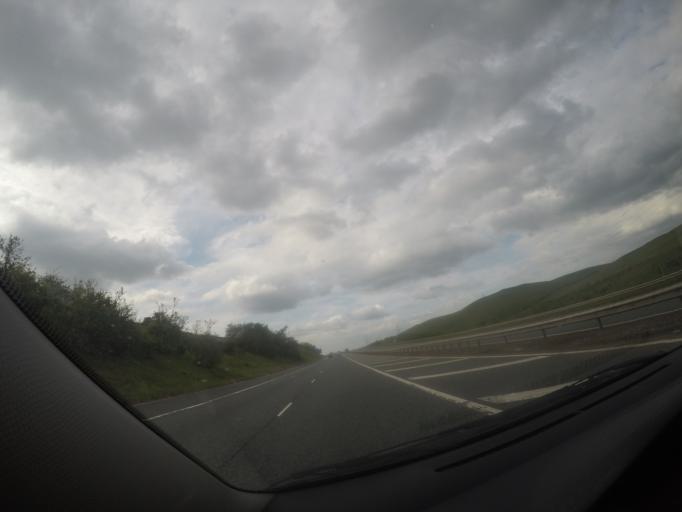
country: GB
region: Scotland
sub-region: South Lanarkshire
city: Douglas
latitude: 55.5533
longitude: -3.8014
